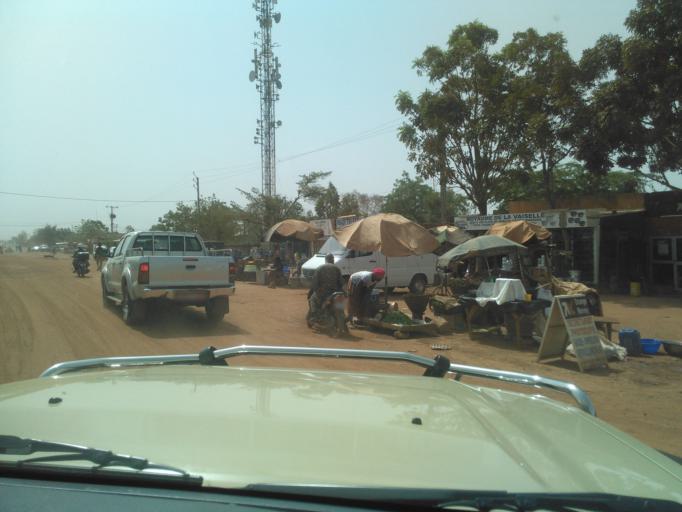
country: BF
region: Centre
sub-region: Kadiogo Province
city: Ouagadougou
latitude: 12.3890
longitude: -1.4769
